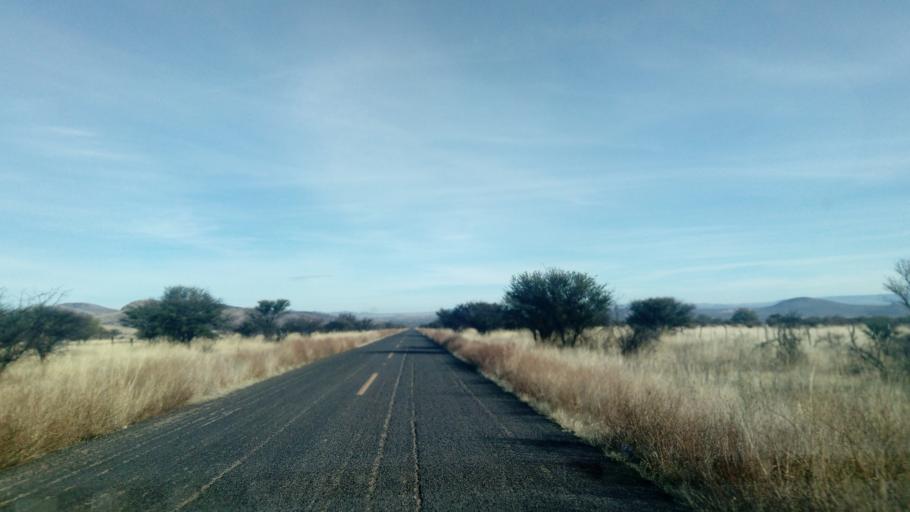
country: MX
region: Durango
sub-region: Nombre de Dios
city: Nombre de Dios
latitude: 23.9236
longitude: -104.3353
